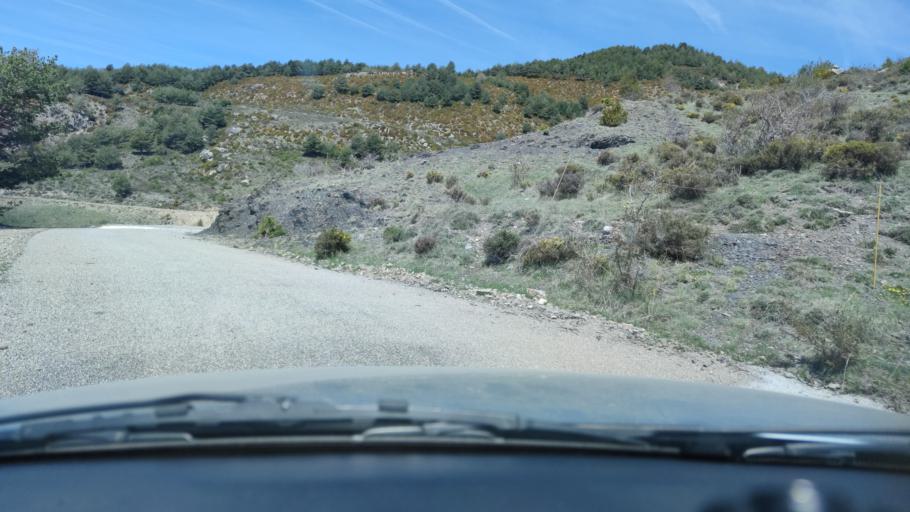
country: ES
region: Catalonia
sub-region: Provincia de Lleida
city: Sort
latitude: 42.3100
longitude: 1.1734
